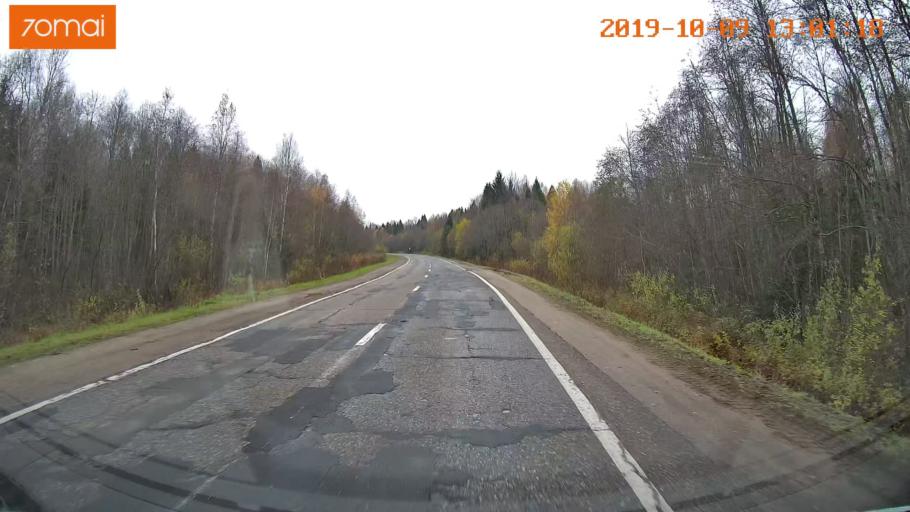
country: RU
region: Jaroslavl
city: Prechistoye
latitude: 58.3695
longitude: 40.4853
